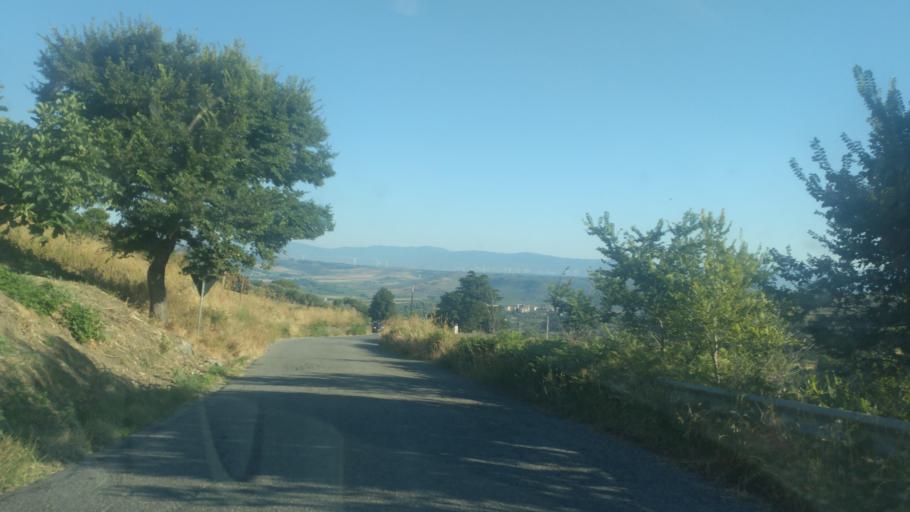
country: IT
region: Calabria
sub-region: Provincia di Catanzaro
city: Montauro
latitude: 38.7637
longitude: 16.5182
